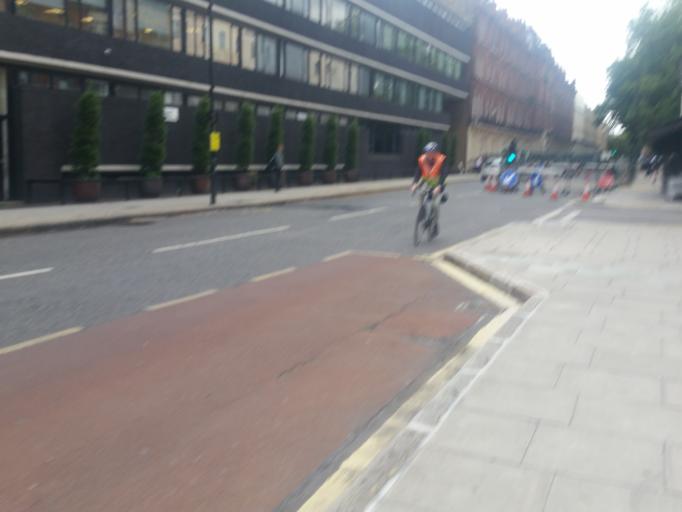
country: GB
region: England
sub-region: Greater London
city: Camden Town
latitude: 51.5254
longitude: -0.1442
